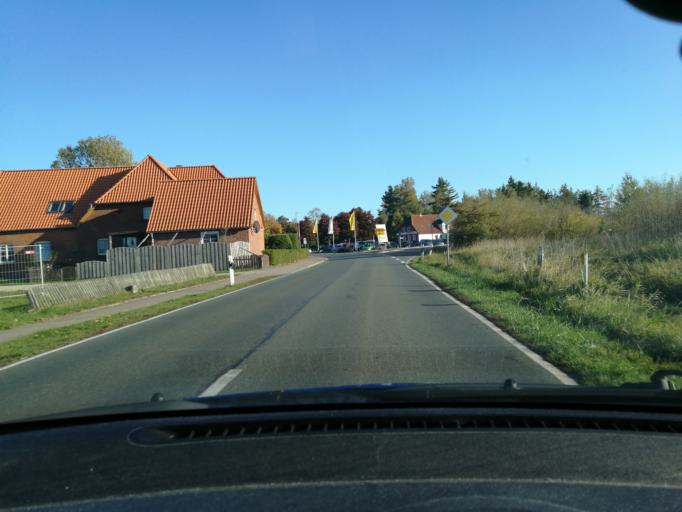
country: DE
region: Lower Saxony
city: Bleckede
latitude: 53.2984
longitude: 10.7142
